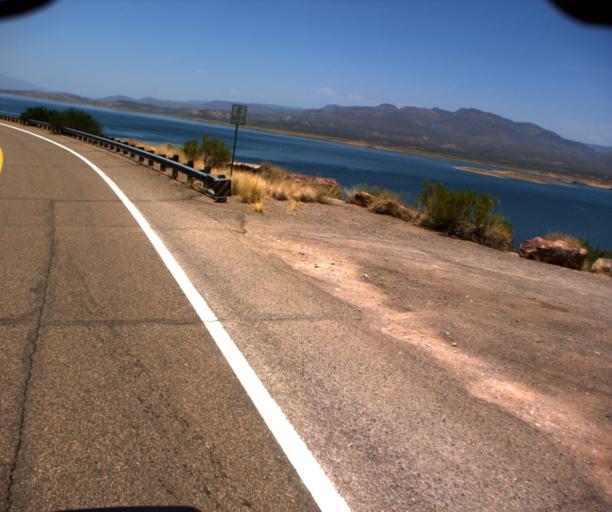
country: US
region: Arizona
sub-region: Gila County
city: Tonto Basin
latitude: 33.6772
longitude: -111.1612
